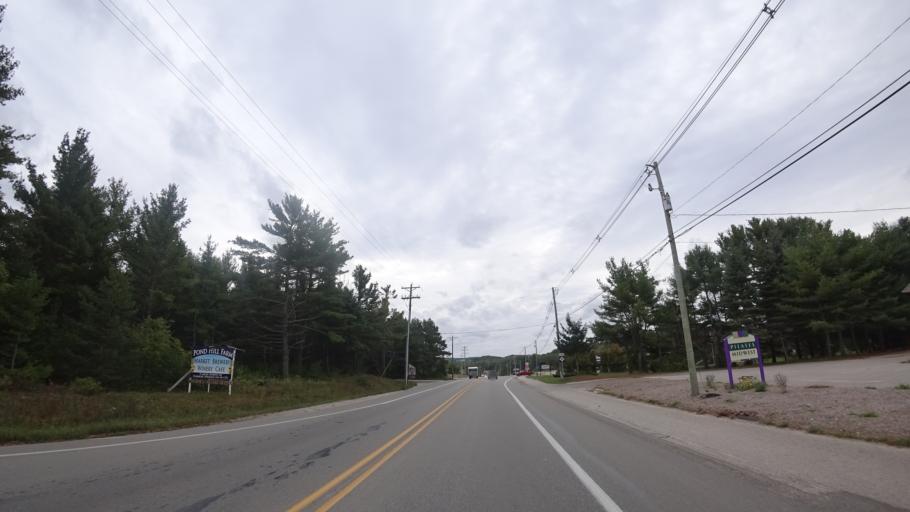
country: US
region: Michigan
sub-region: Emmet County
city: Petoskey
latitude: 45.4217
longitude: -84.9045
